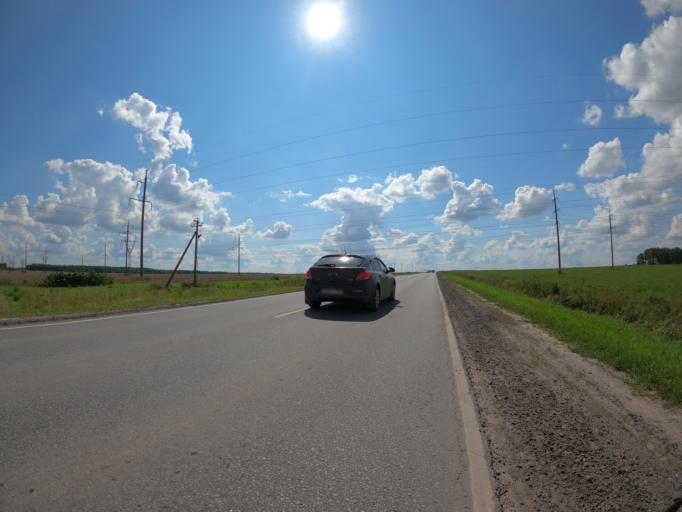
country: RU
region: Moskovskaya
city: Voskresensk
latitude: 55.2887
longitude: 38.6742
